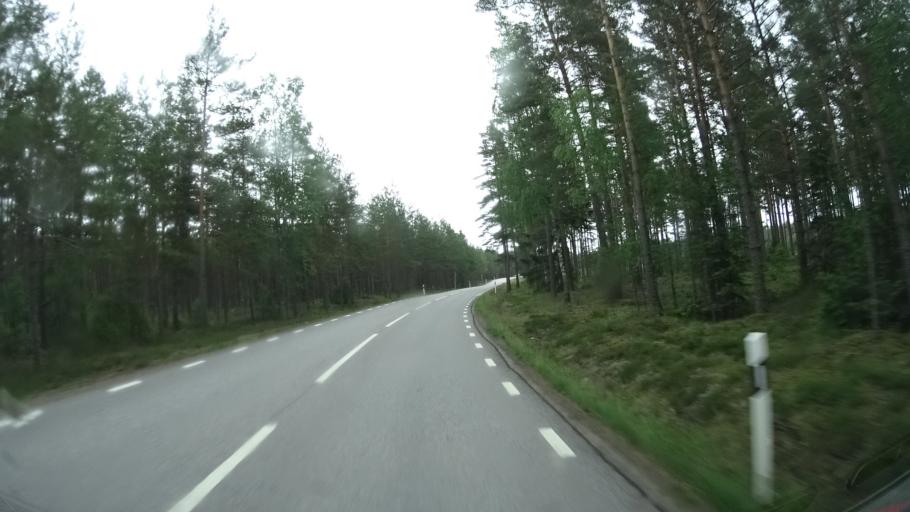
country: SE
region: Kalmar
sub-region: Hultsfreds Kommun
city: Hultsfred
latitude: 57.5276
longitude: 15.7902
